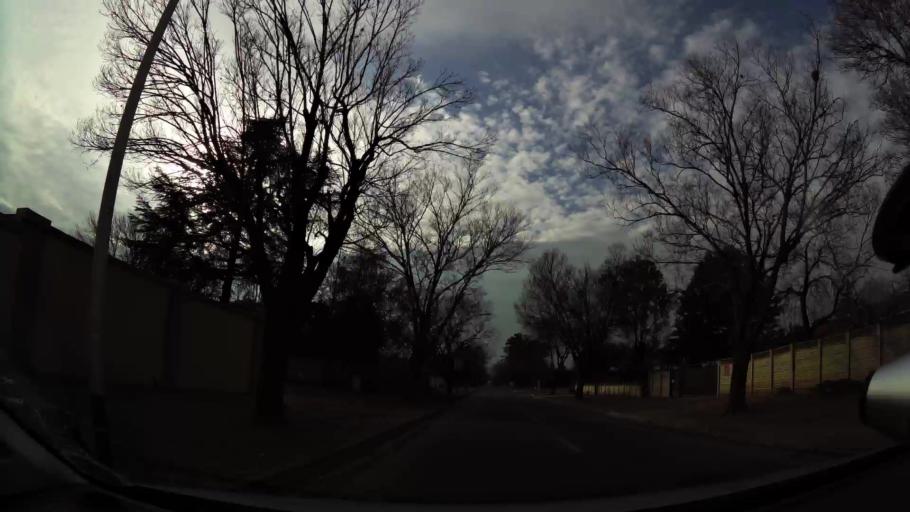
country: ZA
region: Orange Free State
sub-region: Mangaung Metropolitan Municipality
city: Bloemfontein
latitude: -29.1225
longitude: 26.1785
